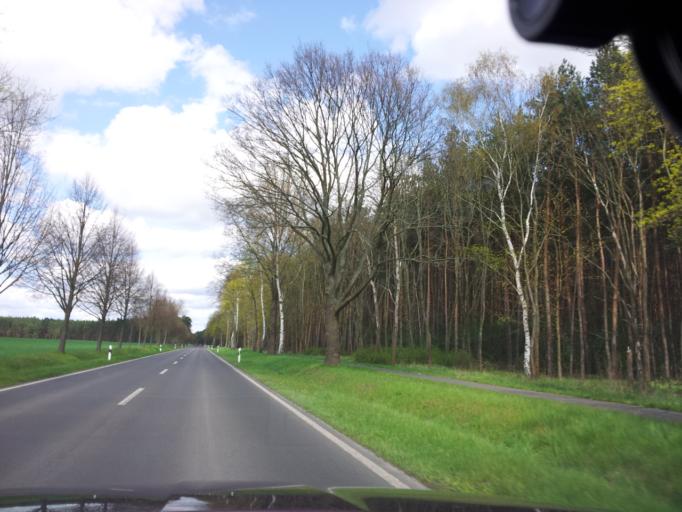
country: DE
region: Brandenburg
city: Rudnitz
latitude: 52.6996
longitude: 13.6090
